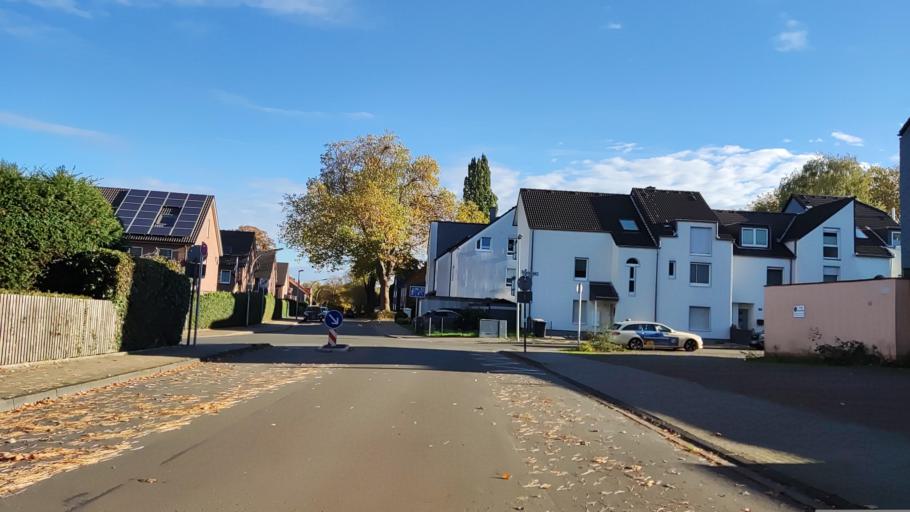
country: DE
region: North Rhine-Westphalia
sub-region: Regierungsbezirk Arnsberg
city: Herne
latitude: 51.5318
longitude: 7.1921
